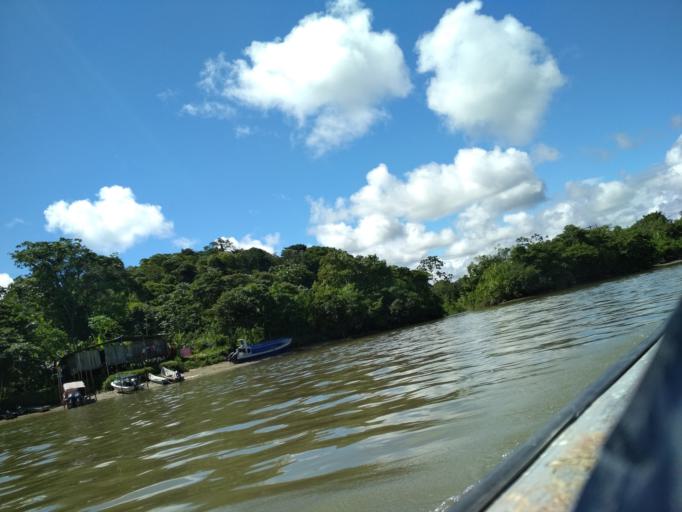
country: CO
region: Cauca
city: Timbiqui
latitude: 2.7692
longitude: -77.6632
